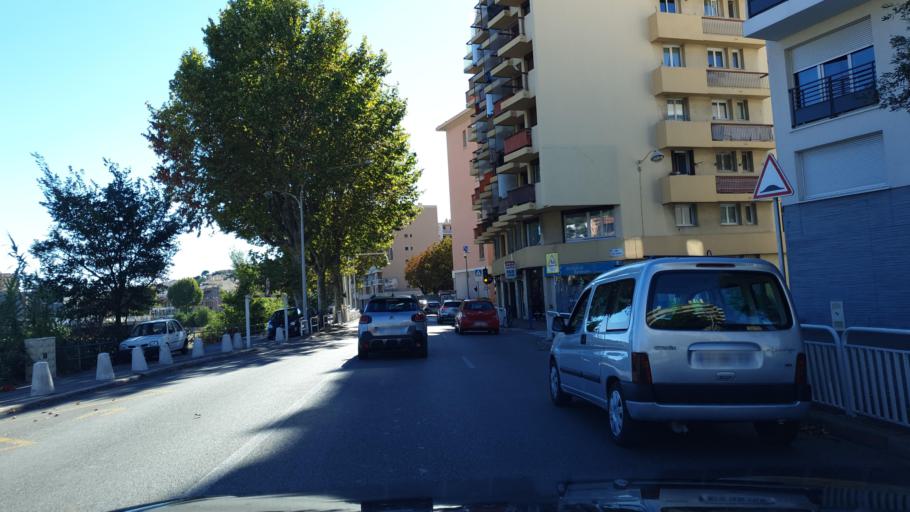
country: FR
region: Provence-Alpes-Cote d'Azur
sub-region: Departement des Alpes-Maritimes
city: Saint-Andre-de-la-Roche
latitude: 43.7194
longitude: 7.2835
